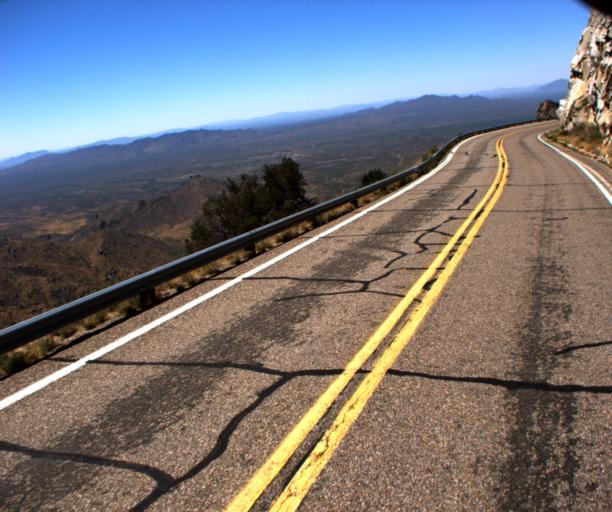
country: US
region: Arizona
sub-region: Pima County
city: Sells
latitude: 31.9508
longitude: -111.6270
